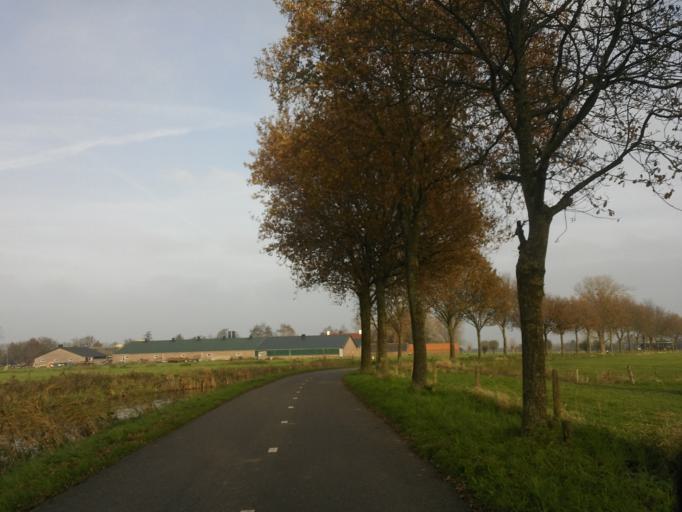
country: NL
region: Utrecht
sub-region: Gemeente Amersfoort
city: Hoogland
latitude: 52.1858
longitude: 5.3397
